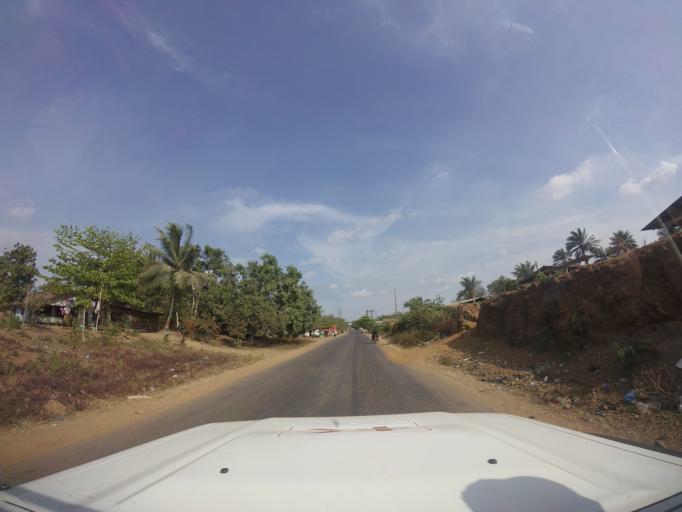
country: LR
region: Bomi
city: Tubmanburg
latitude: 6.7226
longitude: -10.9817
